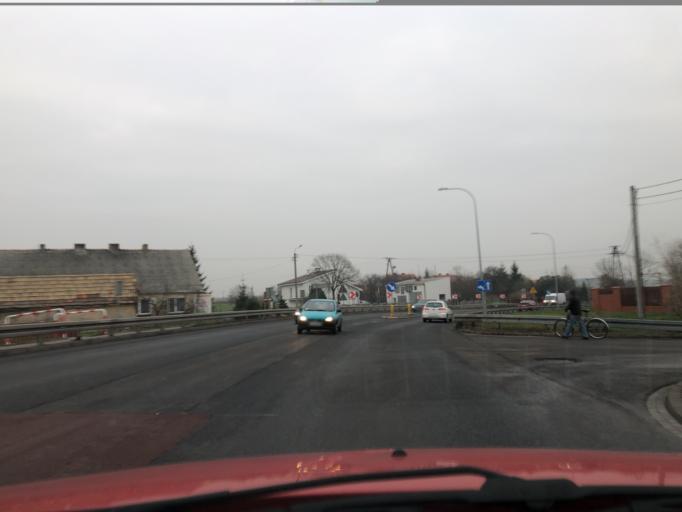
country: PL
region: Greater Poland Voivodeship
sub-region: Powiat jarocinski
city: Witaszyce
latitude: 51.9379
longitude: 17.6036
